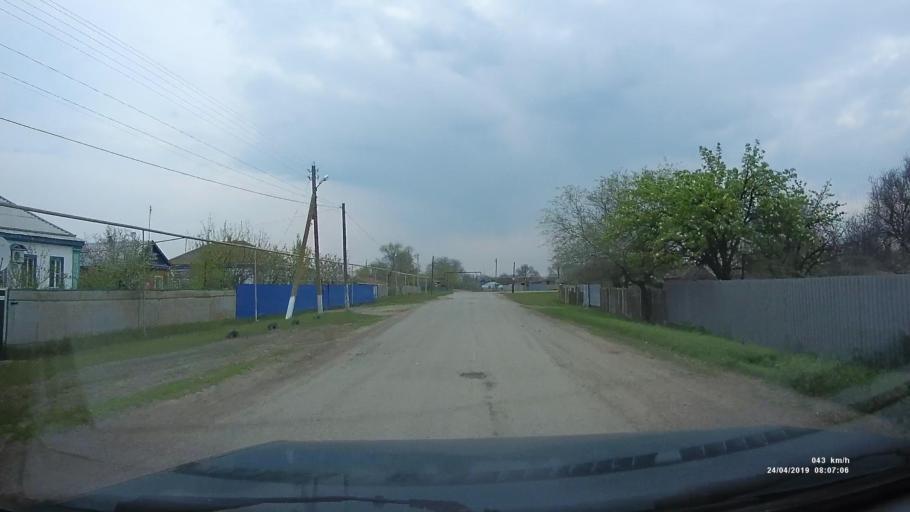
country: RU
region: Kalmykiya
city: Priyutnoye
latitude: 46.1017
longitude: 43.4976
